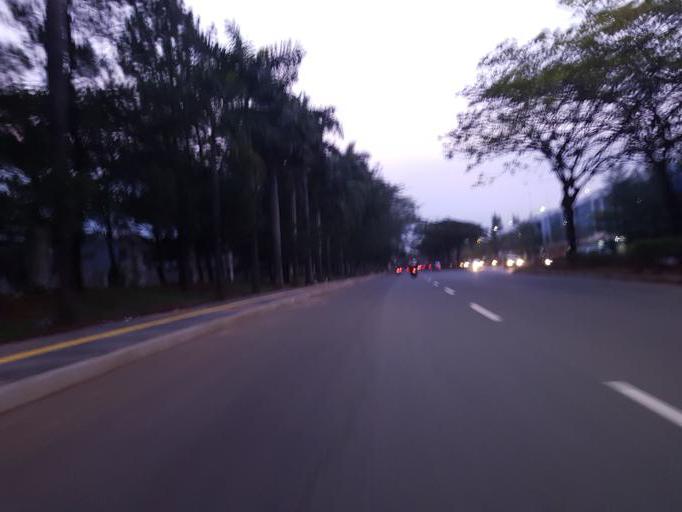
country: ID
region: West Java
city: Serpong
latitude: -6.3314
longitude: 106.6793
